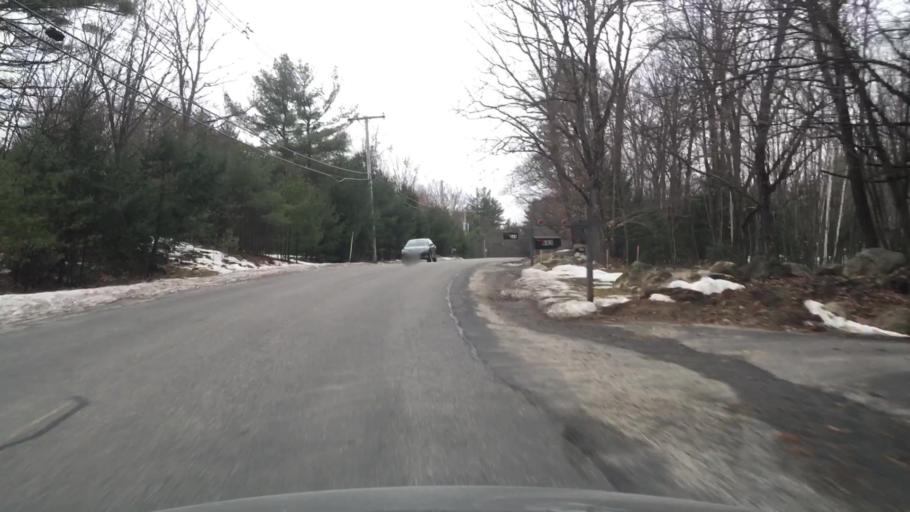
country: US
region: New Hampshire
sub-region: Hillsborough County
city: Goffstown
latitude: 42.9714
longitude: -71.6336
